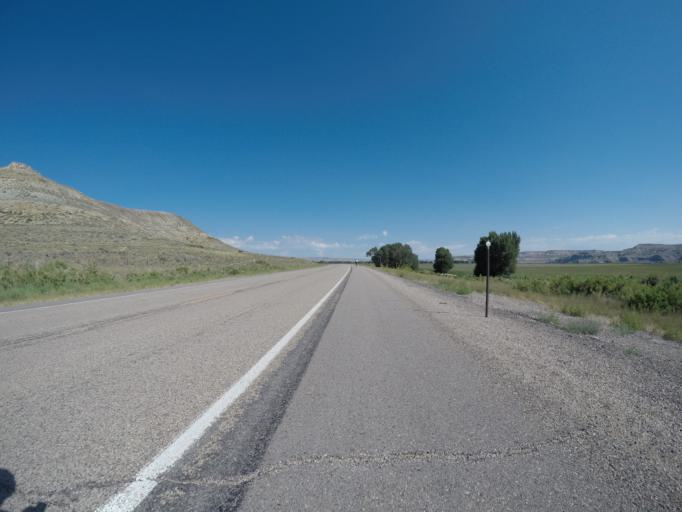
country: US
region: Wyoming
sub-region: Sublette County
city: Marbleton
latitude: 42.2010
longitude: -110.1794
